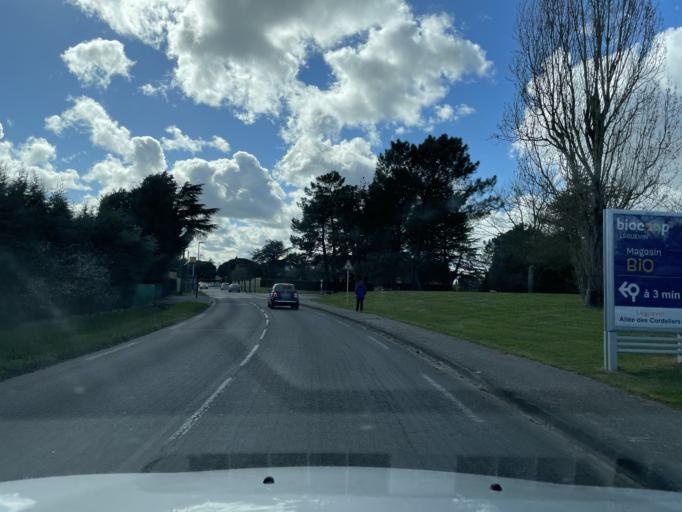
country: FR
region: Midi-Pyrenees
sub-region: Departement de la Haute-Garonne
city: Pibrac
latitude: 43.6130
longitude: 1.2688
